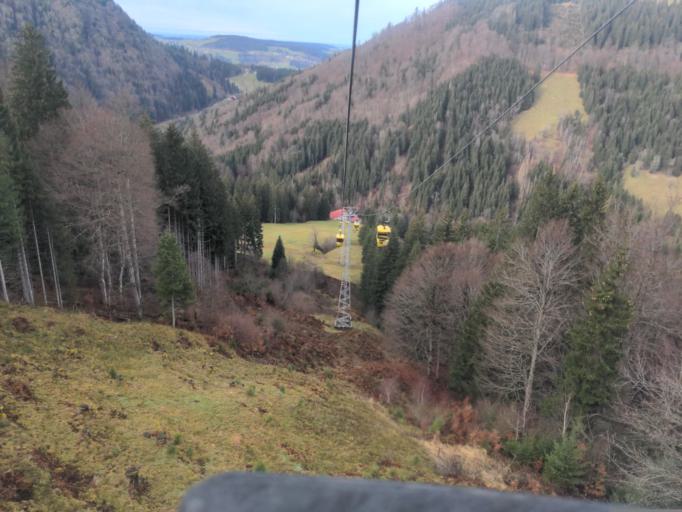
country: DE
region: Bavaria
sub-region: Swabia
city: Balderschwang
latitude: 47.5049
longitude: 10.0620
